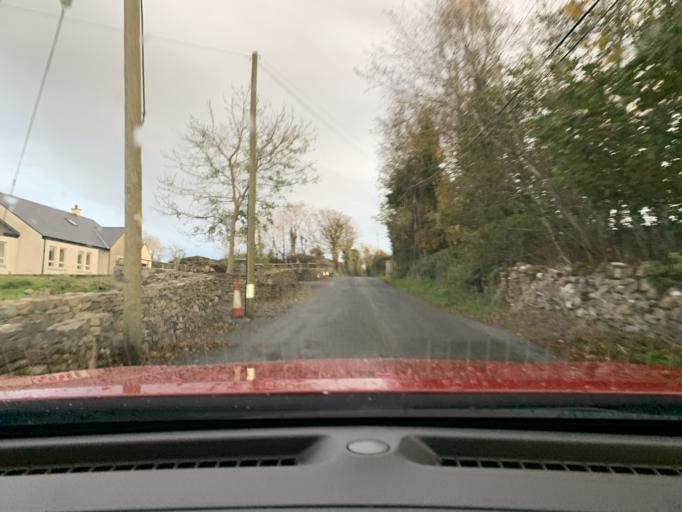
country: IE
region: Connaught
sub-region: Sligo
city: Sligo
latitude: 54.2972
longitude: -8.4887
